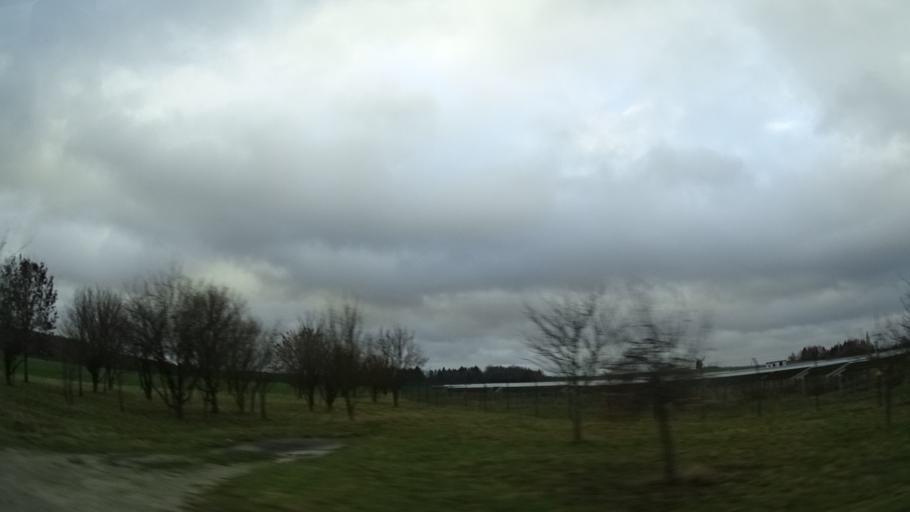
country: DE
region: Thuringia
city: Klettbach
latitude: 50.9212
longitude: 11.1674
